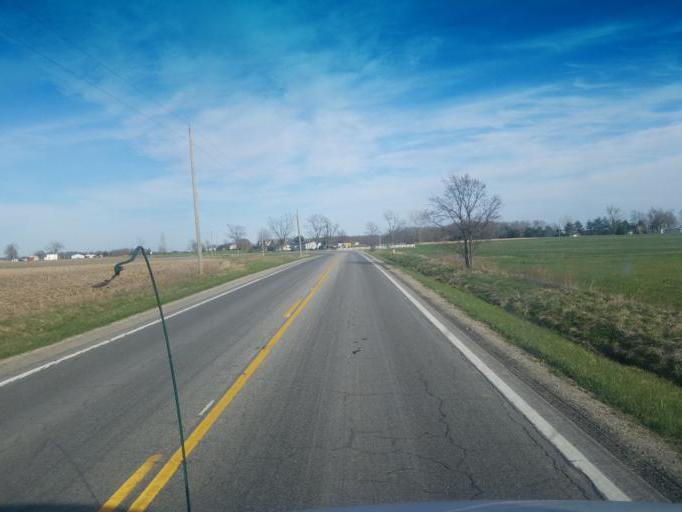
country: US
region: Ohio
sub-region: Shelby County
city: Jackson Center
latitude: 40.3369
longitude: -84.0204
